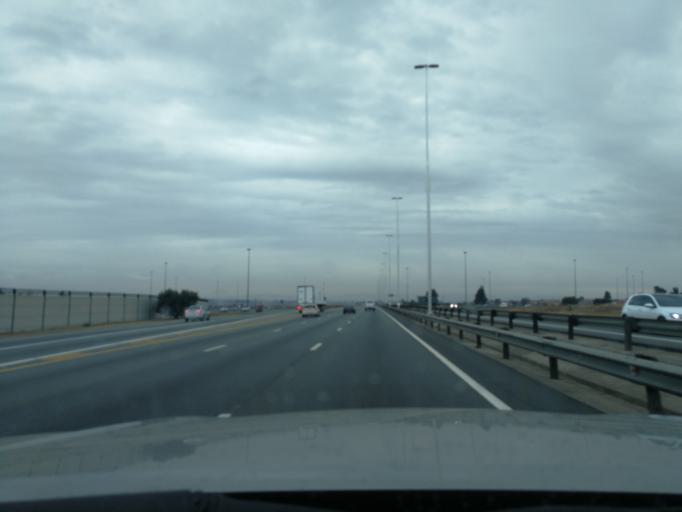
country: ZA
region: Gauteng
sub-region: Ekurhuleni Metropolitan Municipality
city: Germiston
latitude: -26.2853
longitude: 28.1524
